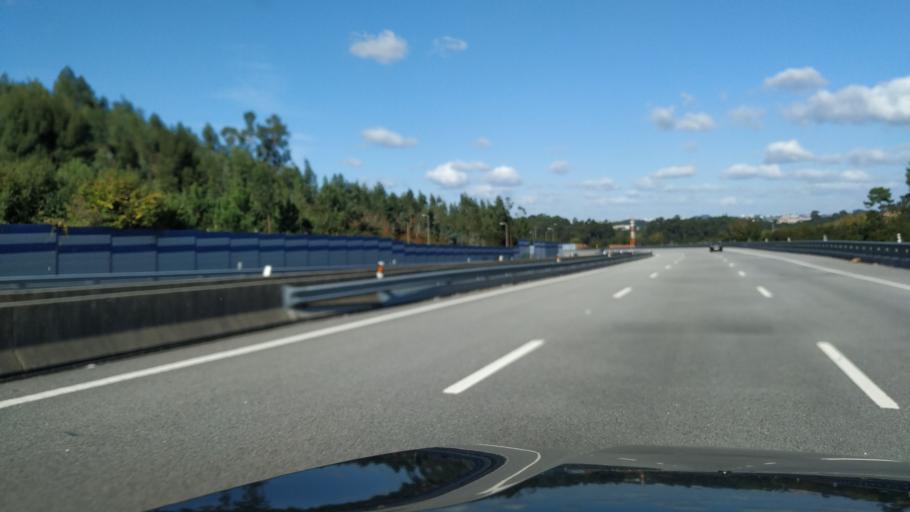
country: PT
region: Porto
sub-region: Vila Nova de Gaia
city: Avintes
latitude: 41.0837
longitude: -8.5514
